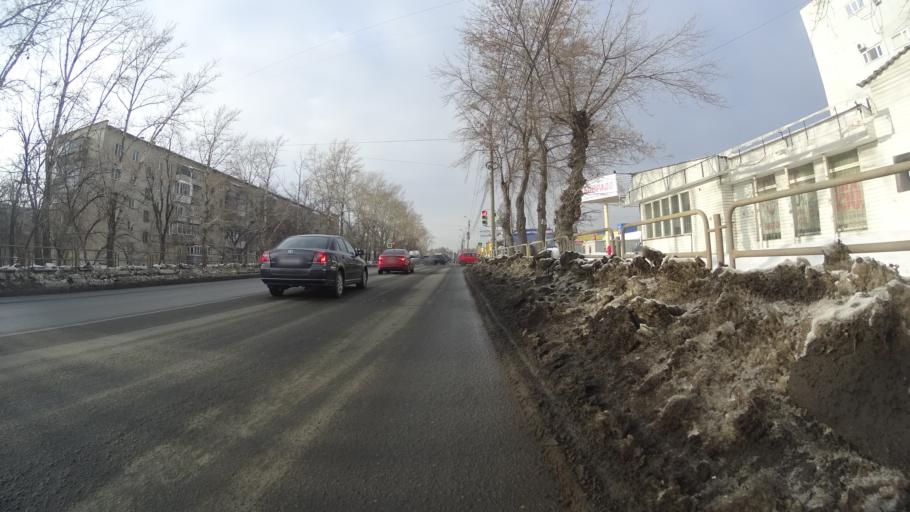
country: RU
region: Chelyabinsk
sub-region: Gorod Chelyabinsk
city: Chelyabinsk
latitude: 55.1248
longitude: 61.3711
